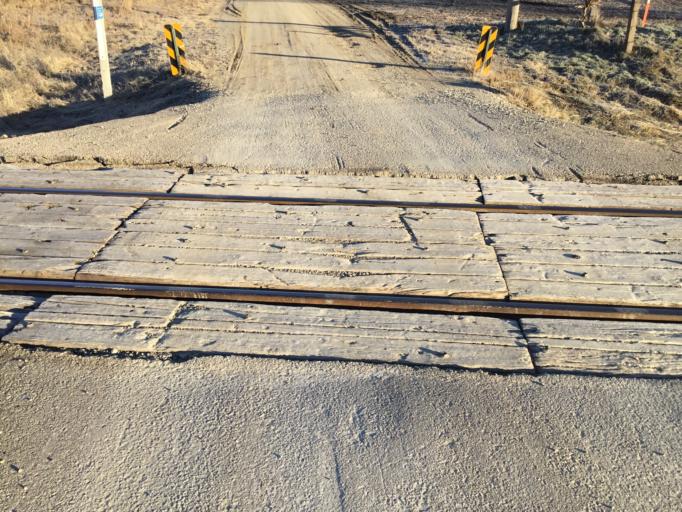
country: US
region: Kansas
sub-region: Shawnee County
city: Silver Lake
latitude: 39.0934
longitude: -95.7716
